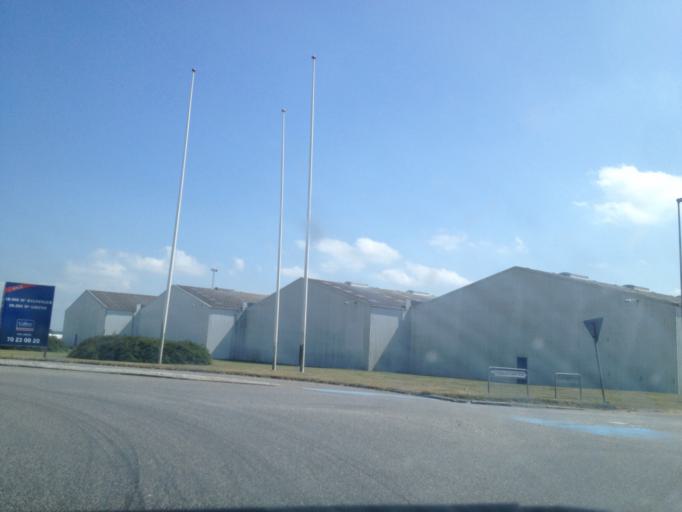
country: DK
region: South Denmark
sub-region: Kolding Kommune
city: Vamdrup
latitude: 55.4371
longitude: 9.3016
